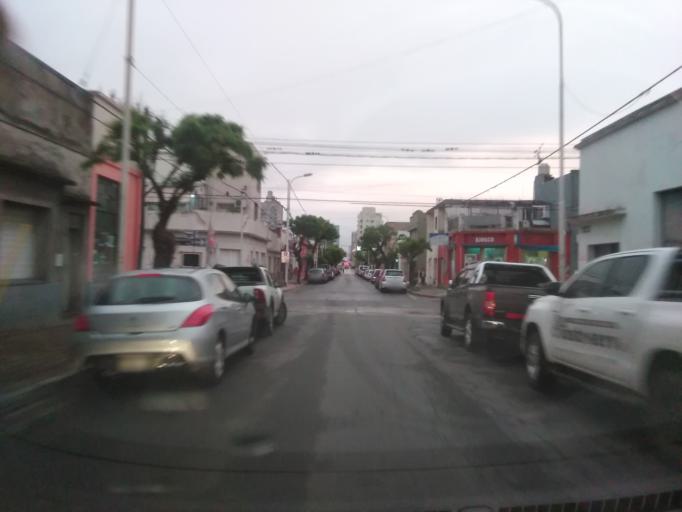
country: AR
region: Buenos Aires
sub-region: Partido de Tandil
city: Tandil
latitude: -37.3273
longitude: -59.1431
